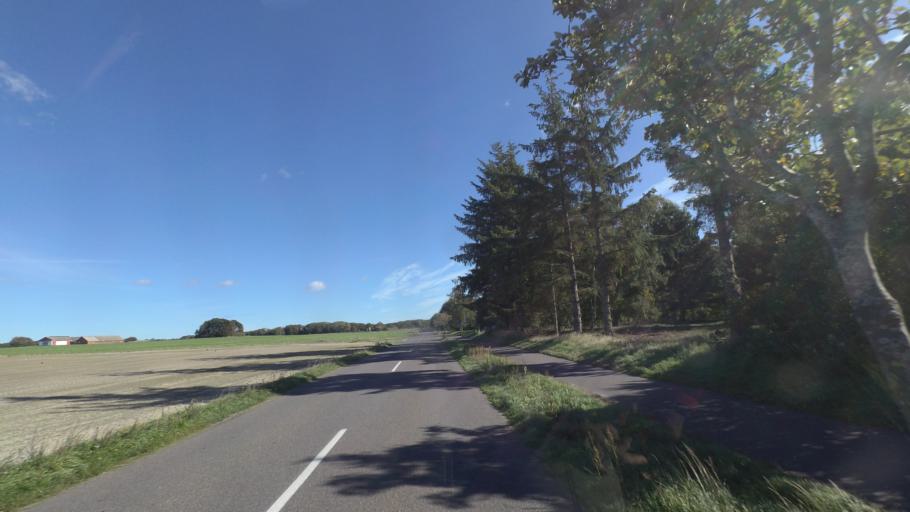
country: DK
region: Capital Region
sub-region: Bornholm Kommune
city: Akirkeby
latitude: 55.0021
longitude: 15.0088
